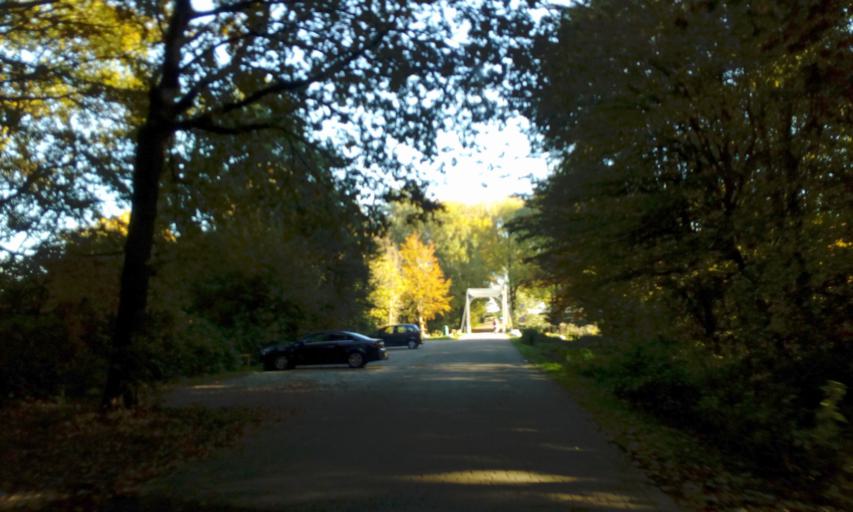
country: NL
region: South Holland
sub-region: Gemeente Lansingerland
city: Bleiswijk
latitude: 51.9995
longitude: 4.5471
